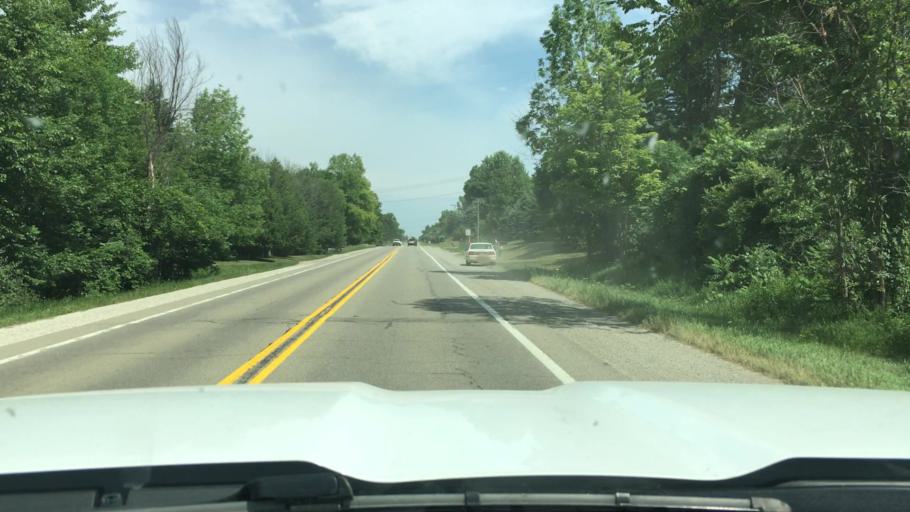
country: US
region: Michigan
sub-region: Sanilac County
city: Brown City
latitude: 43.1633
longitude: -83.0756
